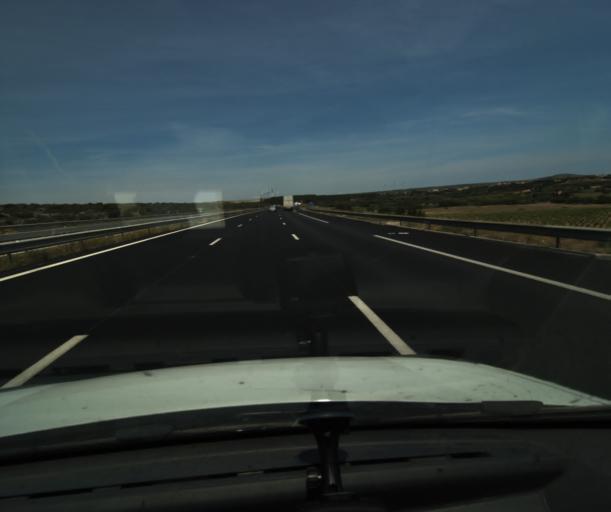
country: FR
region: Languedoc-Roussillon
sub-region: Departement de l'Aude
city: Sigean
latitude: 42.9705
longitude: 2.9700
